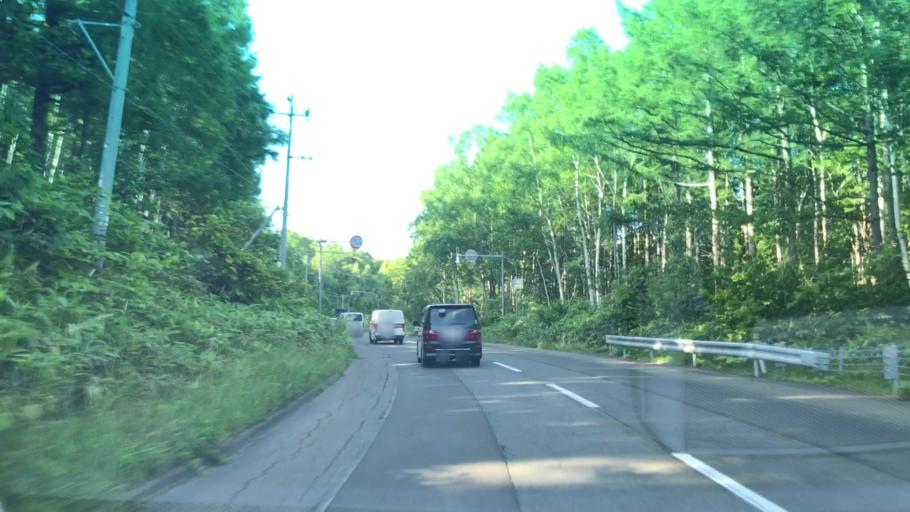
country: JP
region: Hokkaido
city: Otaru
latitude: 43.1262
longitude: 141.0127
